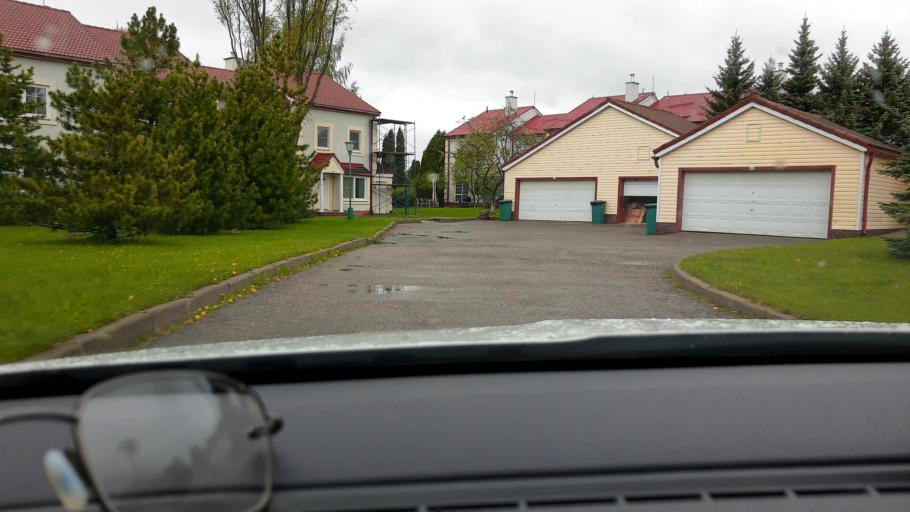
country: RU
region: Moskovskaya
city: Krasnogorsk
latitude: 55.8559
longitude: 37.3131
